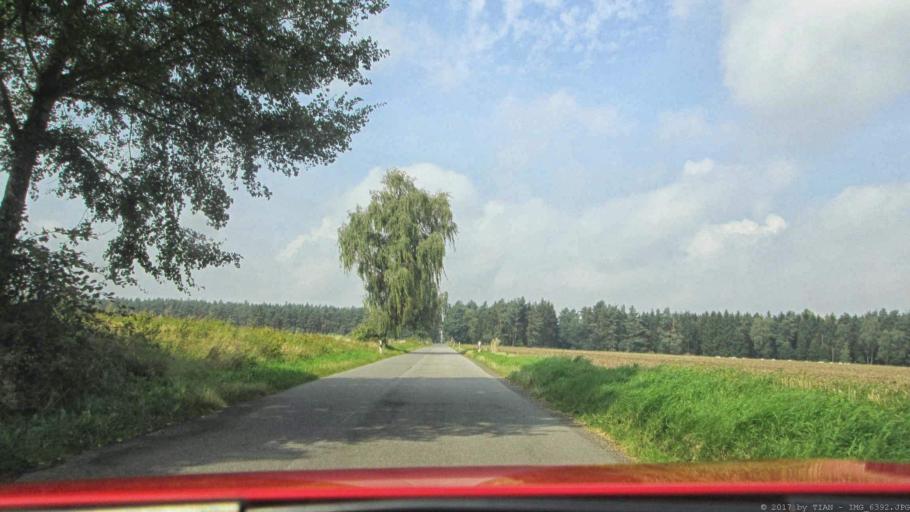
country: DE
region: Lower Saxony
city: Obernholz
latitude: 52.7774
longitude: 10.5839
